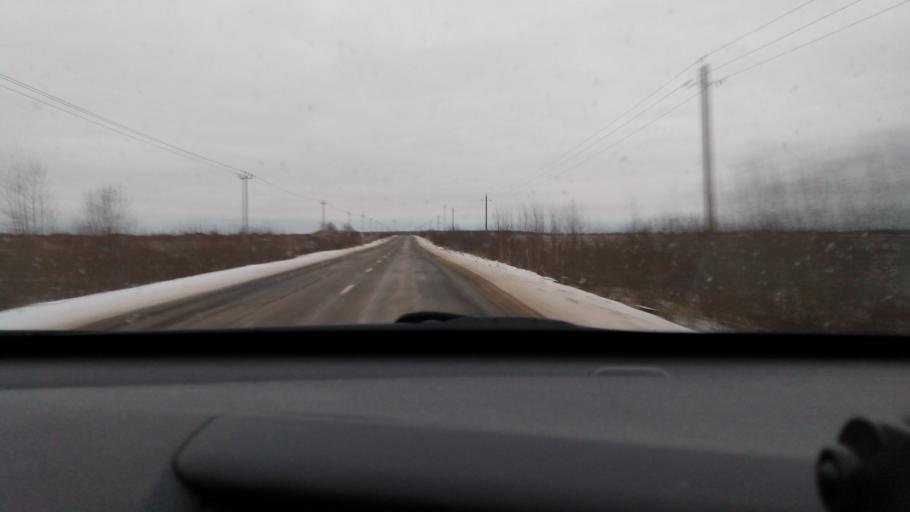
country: RU
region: Moskovskaya
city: Meshcherino
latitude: 55.2901
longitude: 38.3218
